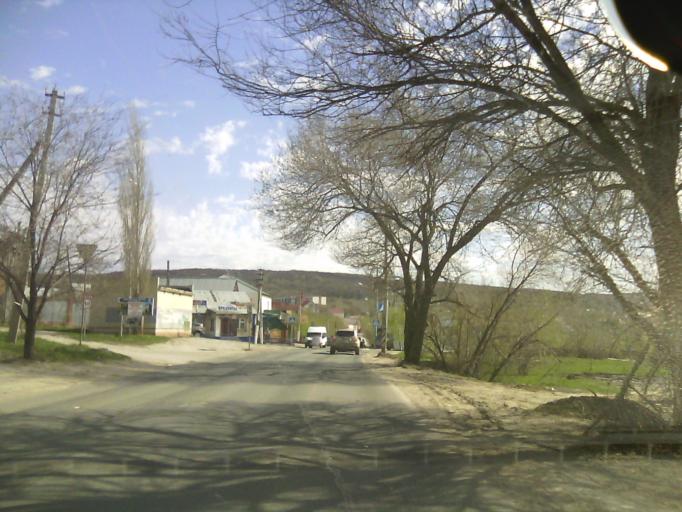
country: RU
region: Saratov
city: Sokolovyy
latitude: 51.5780
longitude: 45.8994
